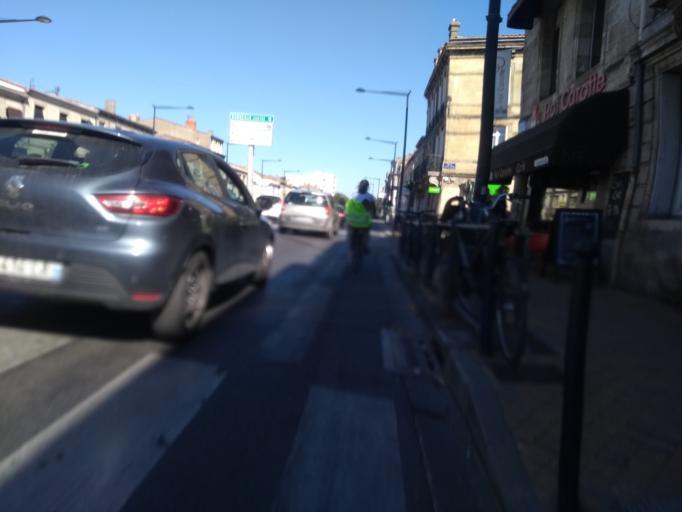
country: FR
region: Aquitaine
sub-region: Departement de la Gironde
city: Le Bouscat
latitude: 44.8530
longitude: -0.5939
